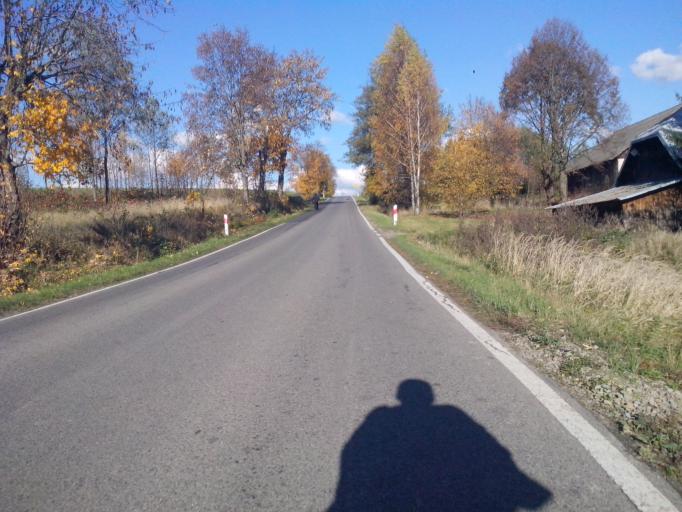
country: PL
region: Subcarpathian Voivodeship
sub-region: Powiat strzyzowski
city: Jawornik
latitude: 49.7934
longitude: 21.8591
